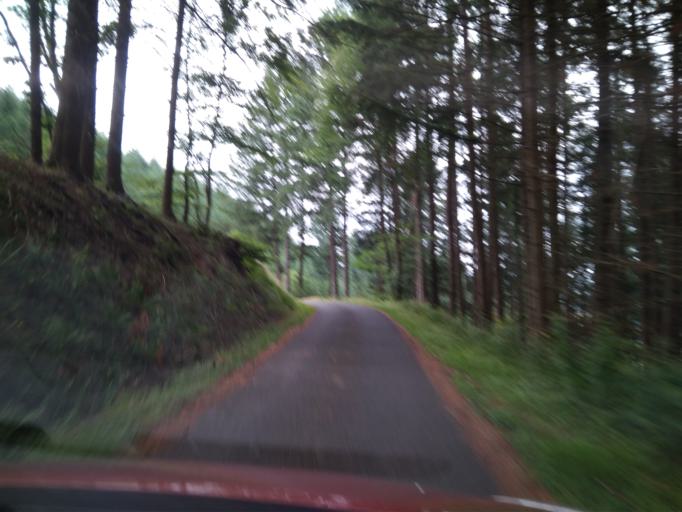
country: FR
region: Rhone-Alpes
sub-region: Departement de la Loire
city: La Pacaudiere
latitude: 46.1380
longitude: 3.7927
